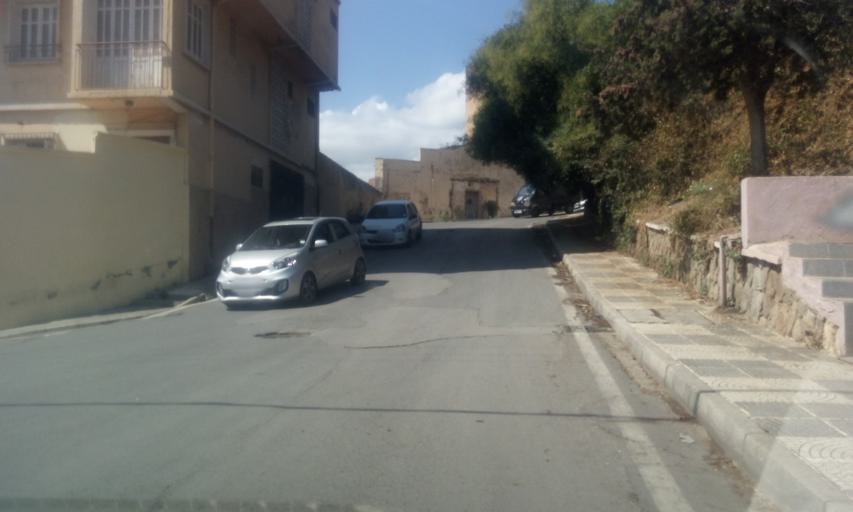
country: DZ
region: Bejaia
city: Bejaia
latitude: 36.7570
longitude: 5.0876
